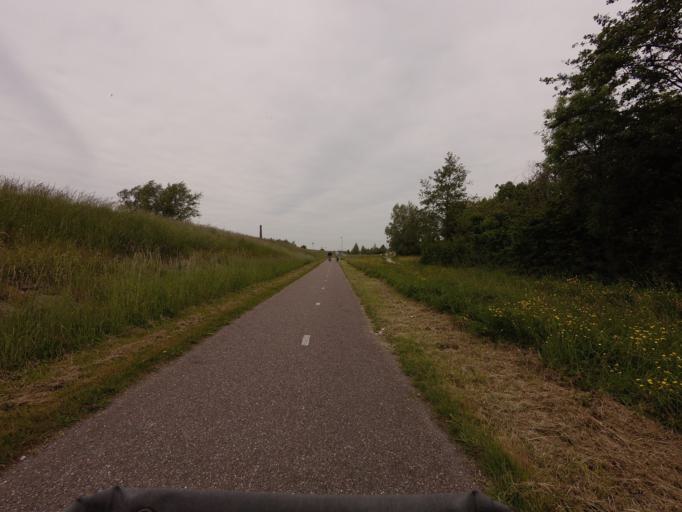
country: NL
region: North Holland
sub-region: Gemeente Medemblik
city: Medemblik
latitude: 52.7570
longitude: 5.1208
